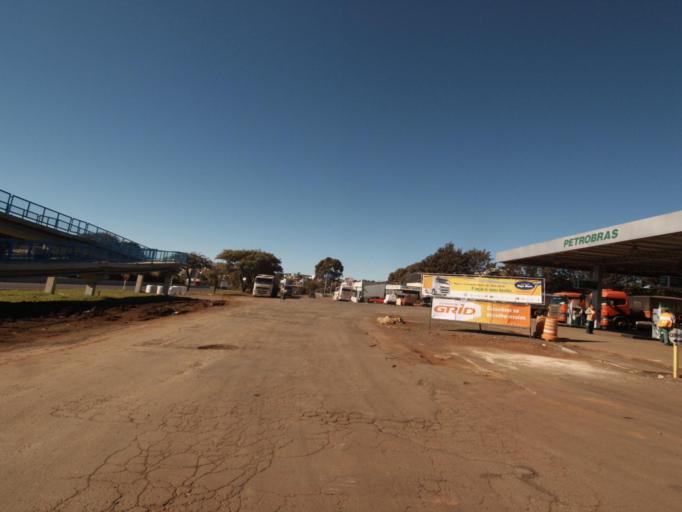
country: BR
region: Santa Catarina
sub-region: Xanxere
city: Xanxere
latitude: -26.8848
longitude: -52.4094
